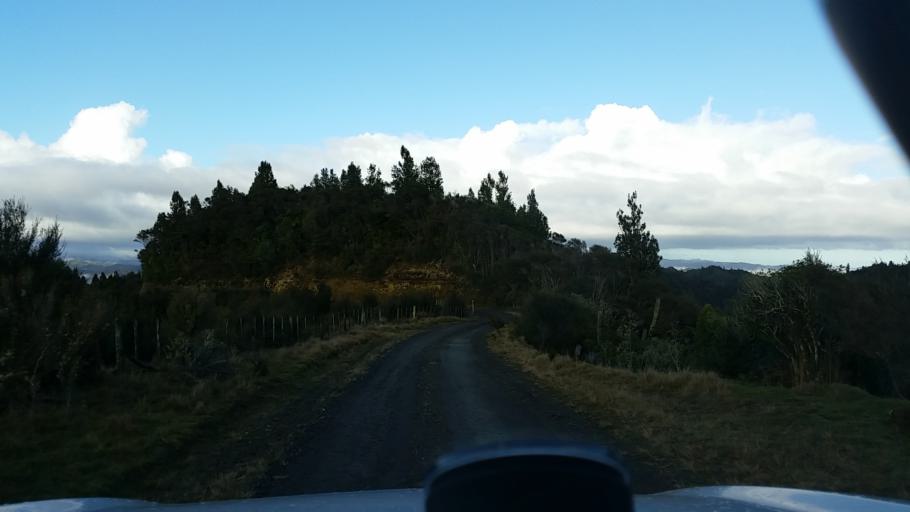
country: NZ
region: Taranaki
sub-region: South Taranaki District
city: Eltham
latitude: -39.4218
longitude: 174.5570
